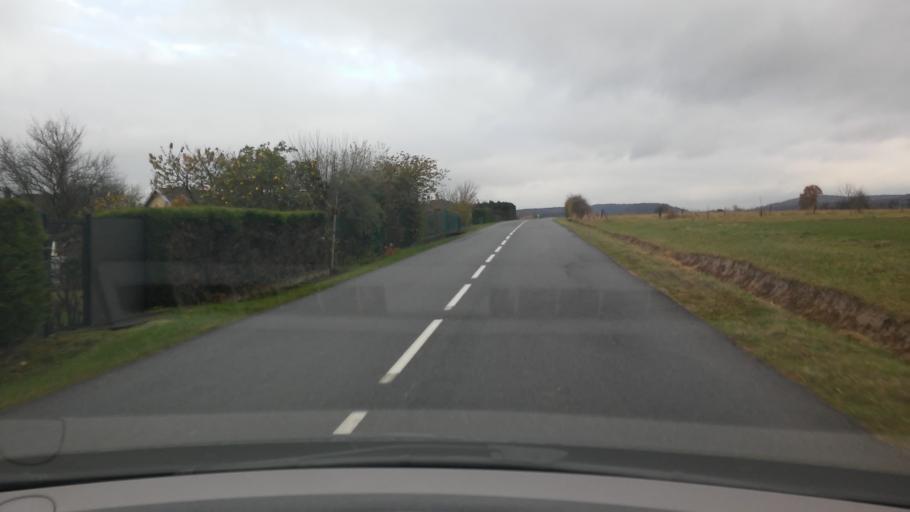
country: FR
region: Lorraine
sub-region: Departement de la Moselle
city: Kedange-sur-Canner
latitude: 49.3011
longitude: 6.3144
